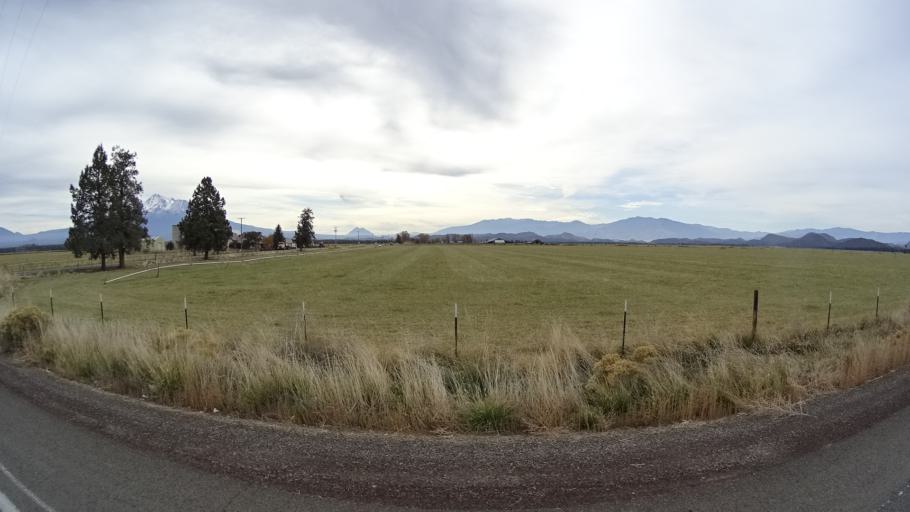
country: US
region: California
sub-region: Siskiyou County
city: Montague
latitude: 41.6238
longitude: -122.4001
